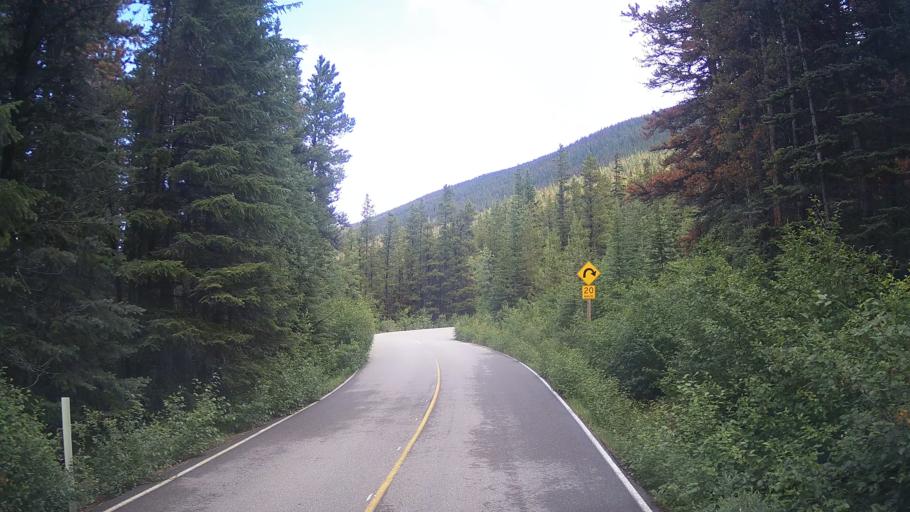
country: CA
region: Alberta
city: Jasper Park Lodge
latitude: 52.7306
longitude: -118.0496
